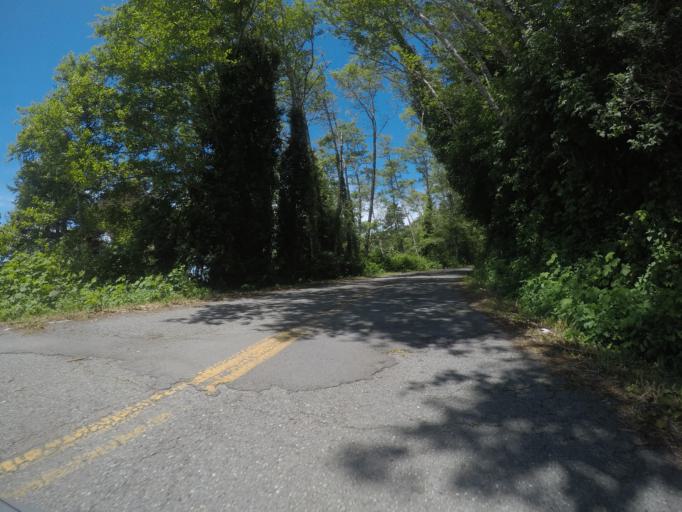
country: US
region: California
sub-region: Del Norte County
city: Bertsch-Oceanview
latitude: 41.5478
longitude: -124.0758
